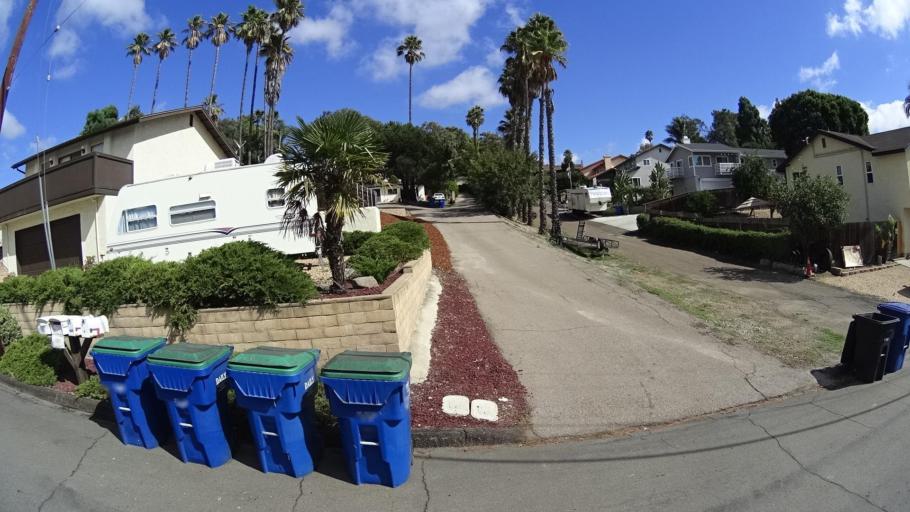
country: US
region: California
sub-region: San Diego County
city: Casa de Oro-Mount Helix
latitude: 32.7429
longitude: -116.9633
